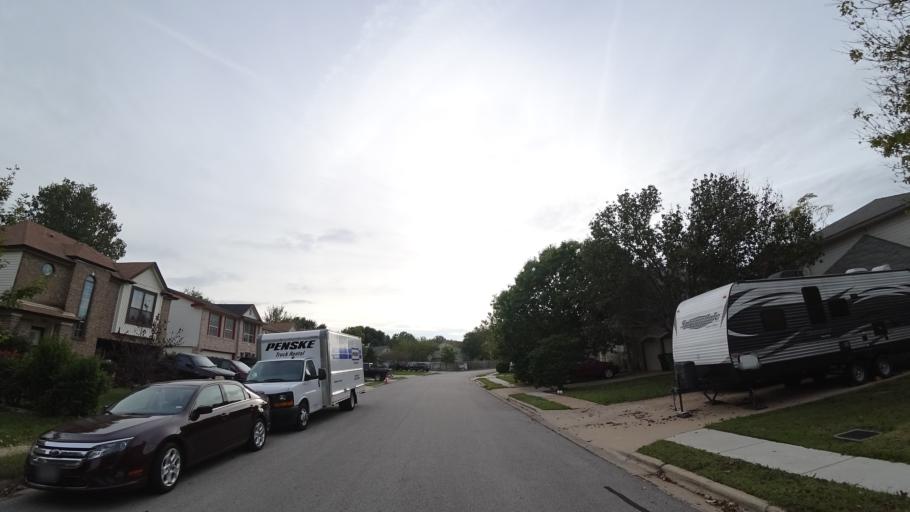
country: US
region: Texas
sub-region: Williamson County
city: Round Rock
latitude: 30.5049
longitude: -97.6651
